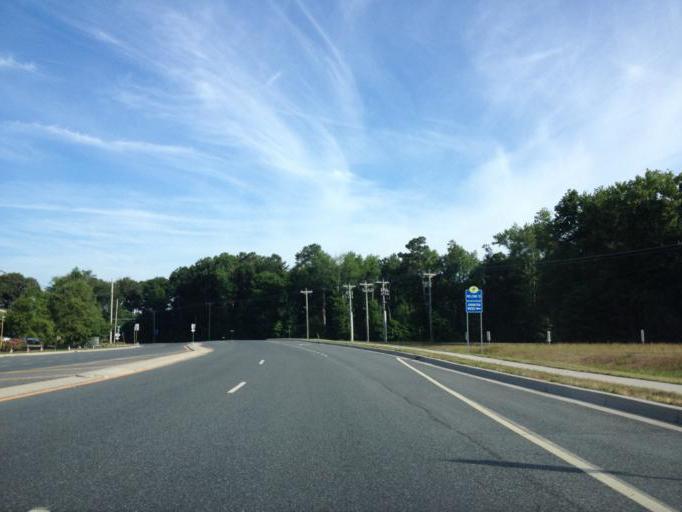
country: US
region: Delaware
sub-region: Sussex County
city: Ocean View
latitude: 38.4705
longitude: -75.1164
